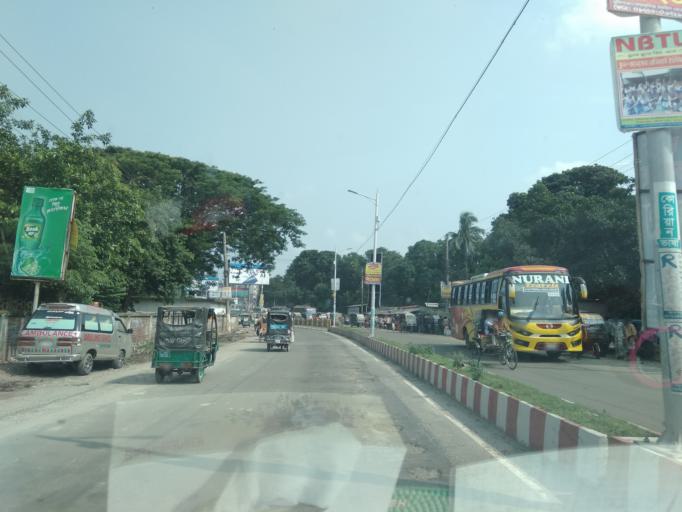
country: BD
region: Rangpur Division
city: Rangpur
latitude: 25.7672
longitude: 89.2300
